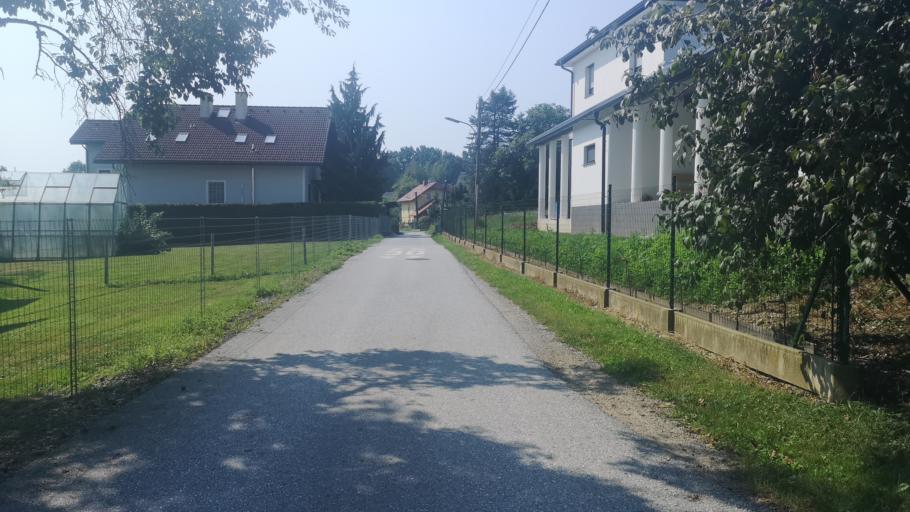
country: AT
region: Styria
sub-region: Politischer Bezirk Graz-Umgebung
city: Seiersberg
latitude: 46.9851
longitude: 15.3936
